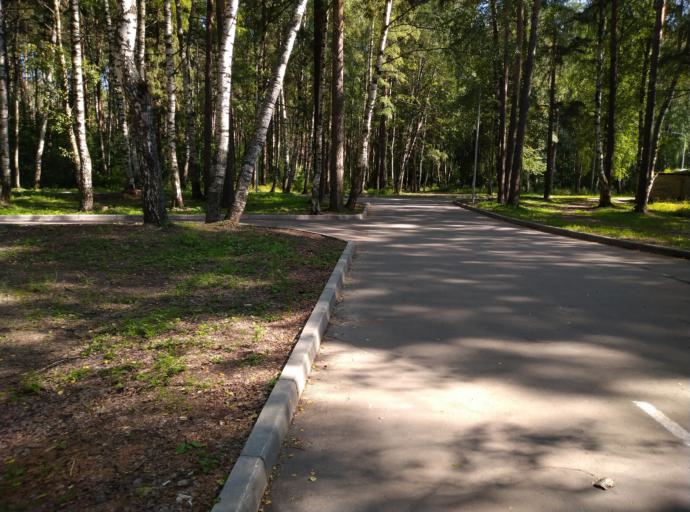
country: RU
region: Kostroma
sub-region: Kostromskoy Rayon
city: Kostroma
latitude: 57.7932
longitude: 40.9649
